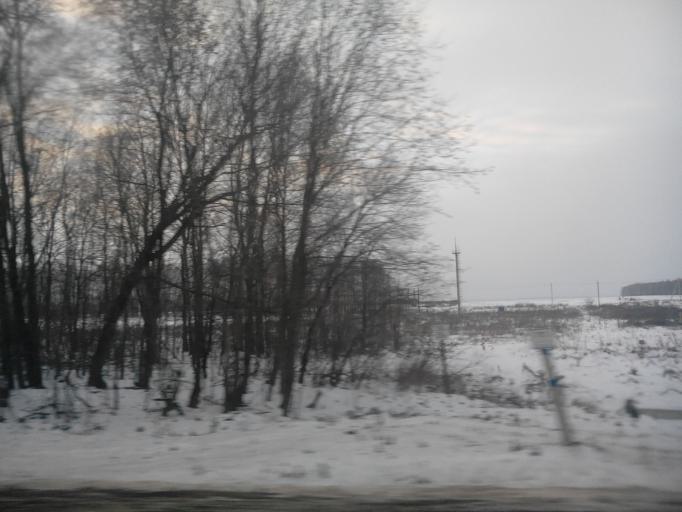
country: RU
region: Tula
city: Shchekino
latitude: 53.8630
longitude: 37.4367
